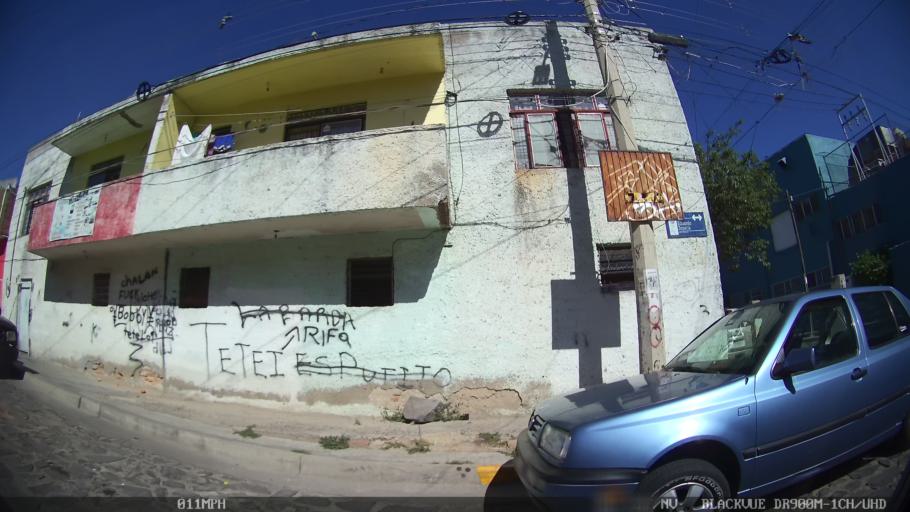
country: MX
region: Jalisco
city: Tlaquepaque
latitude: 20.6802
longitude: -103.2775
